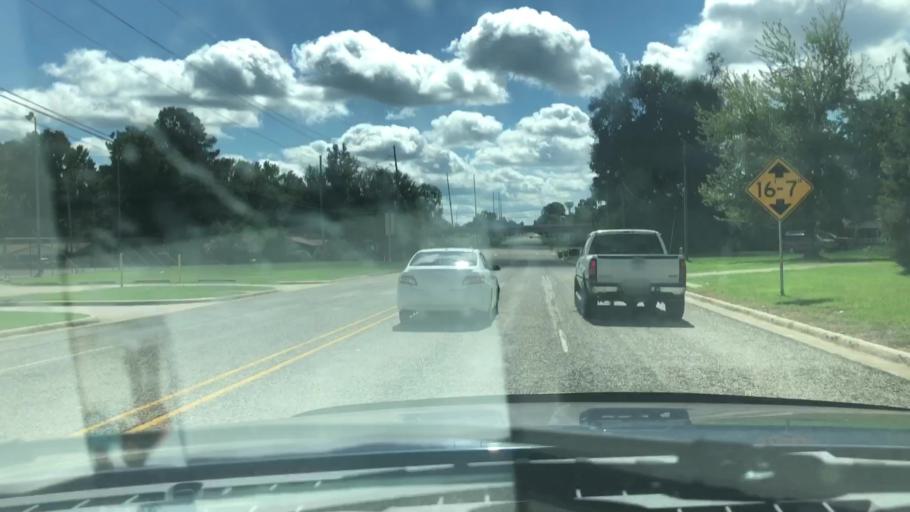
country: US
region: Texas
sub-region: Bowie County
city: Wake Village
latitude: 33.3899
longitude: -94.0922
